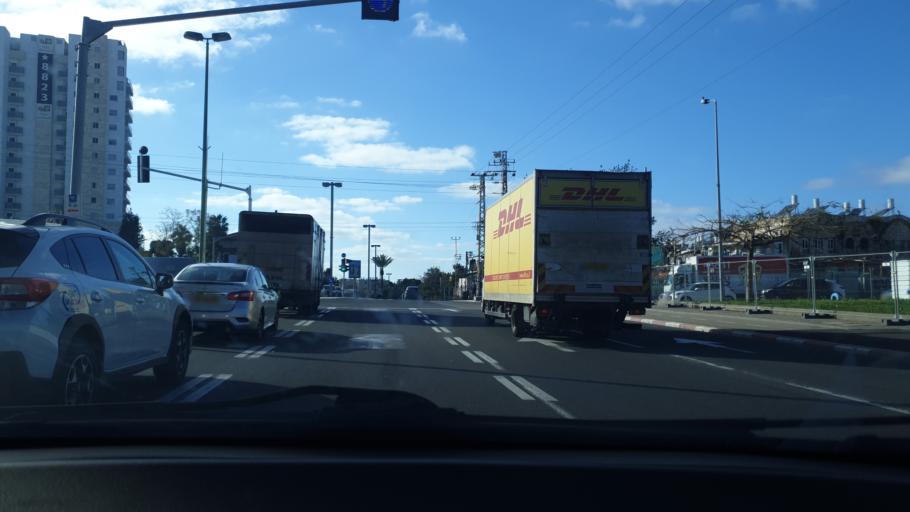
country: IL
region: Tel Aviv
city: Yafo
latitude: 32.0428
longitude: 34.7714
